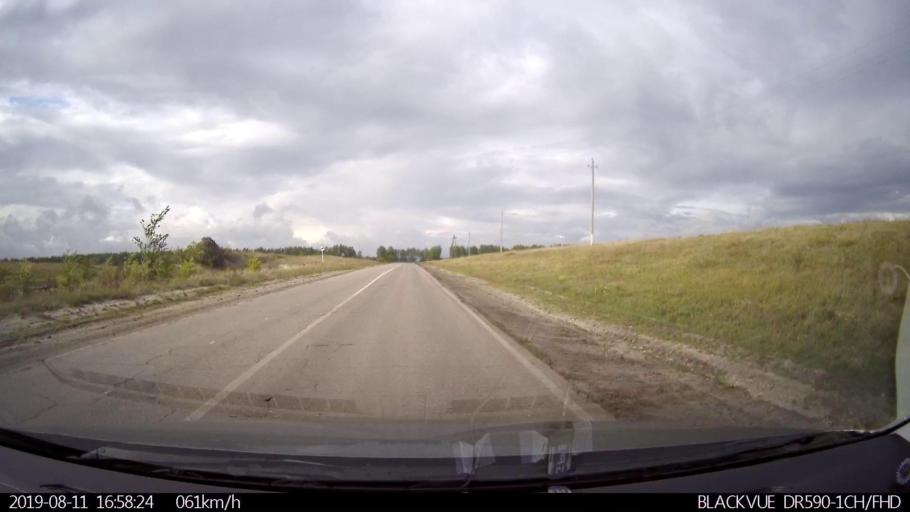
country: RU
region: Ulyanovsk
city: Mayna
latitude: 54.3080
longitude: 47.6561
